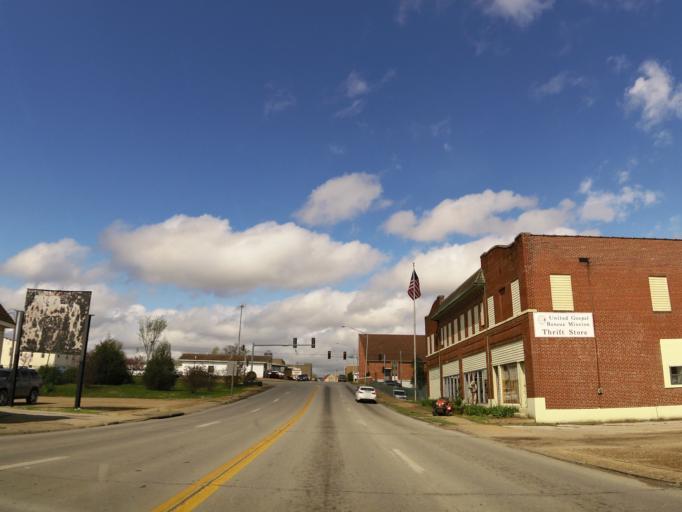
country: US
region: Missouri
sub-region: Butler County
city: Poplar Bluff
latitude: 36.7571
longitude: -90.3942
